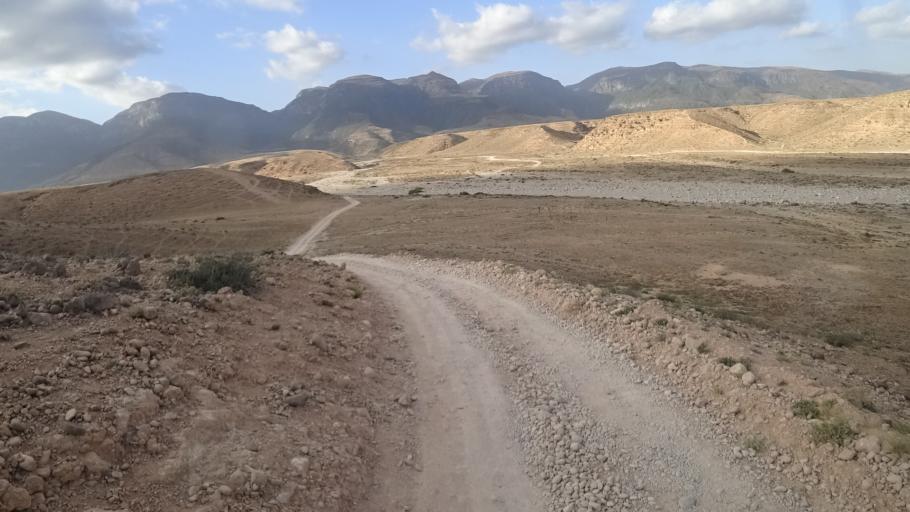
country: OM
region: Zufar
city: Salalah
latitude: 16.9745
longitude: 53.8532
